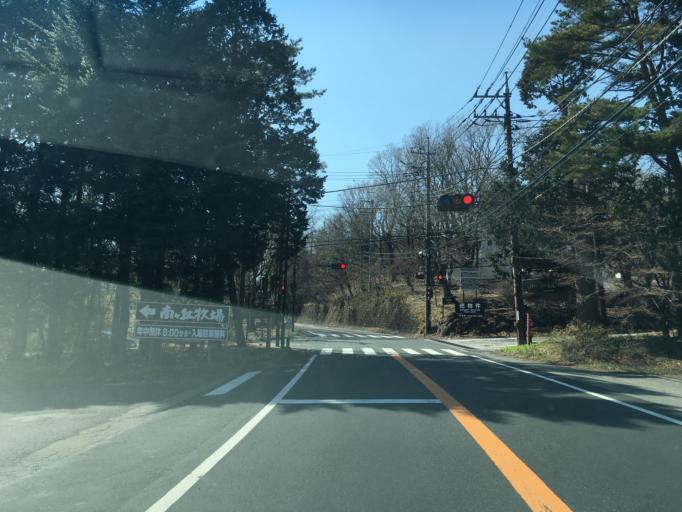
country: JP
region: Tochigi
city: Kuroiso
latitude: 37.0798
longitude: 140.0005
